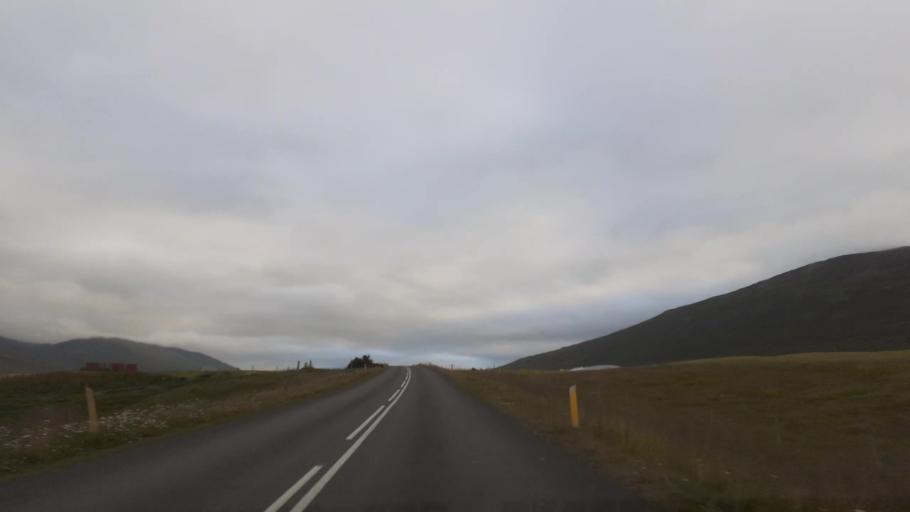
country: IS
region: Northeast
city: Dalvik
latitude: 65.9562
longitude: -18.5494
